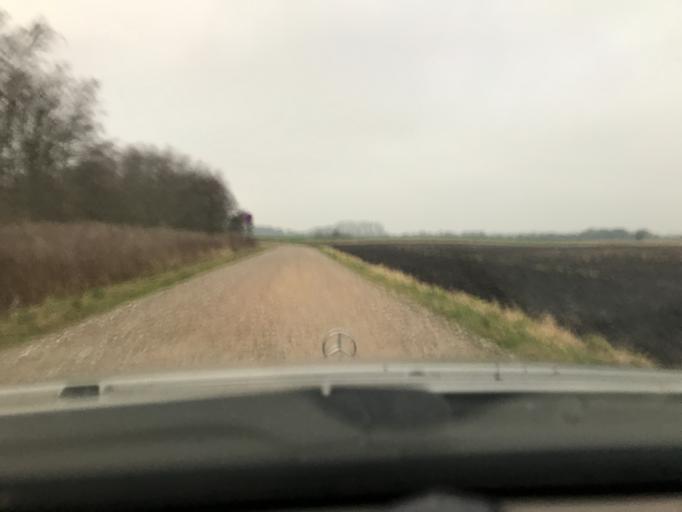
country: DK
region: South Denmark
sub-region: Sonderborg Kommune
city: Horuphav
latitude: 54.8679
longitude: 10.0034
